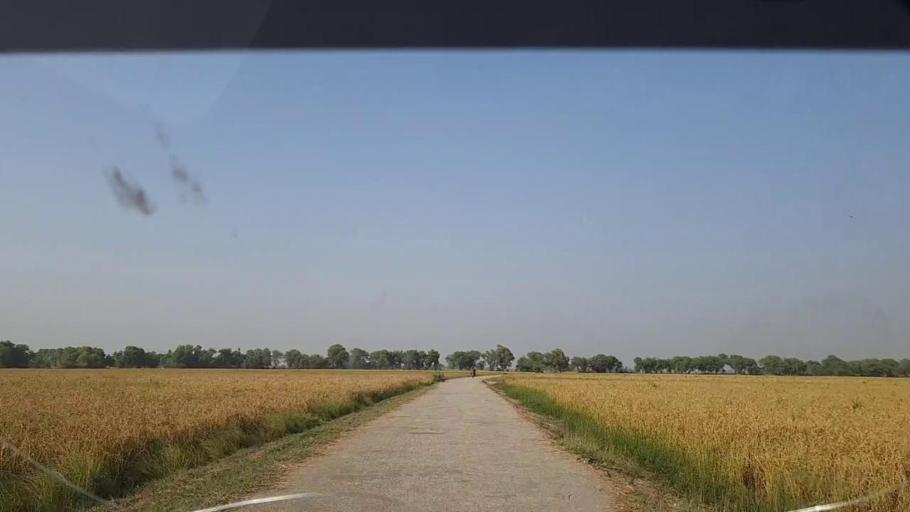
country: PK
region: Sindh
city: Shikarpur
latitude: 28.1204
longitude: 68.5832
